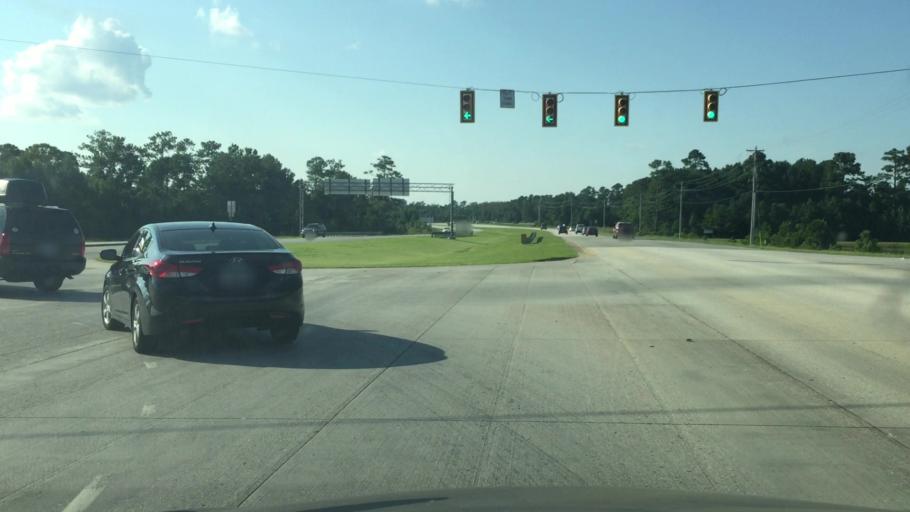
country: US
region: South Carolina
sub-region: Horry County
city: North Myrtle Beach
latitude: 33.8456
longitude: -78.7019
